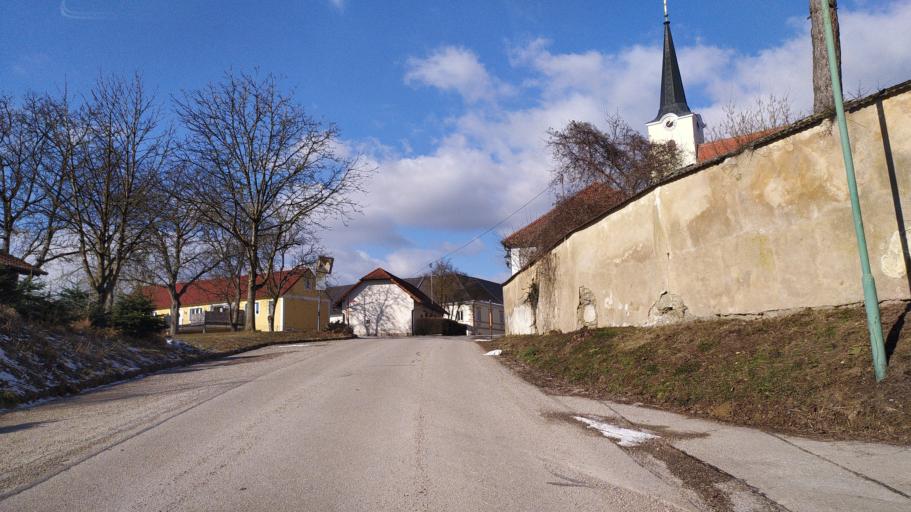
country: AT
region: Lower Austria
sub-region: Politischer Bezirk Amstetten
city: Strengberg
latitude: 48.1572
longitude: 14.7170
